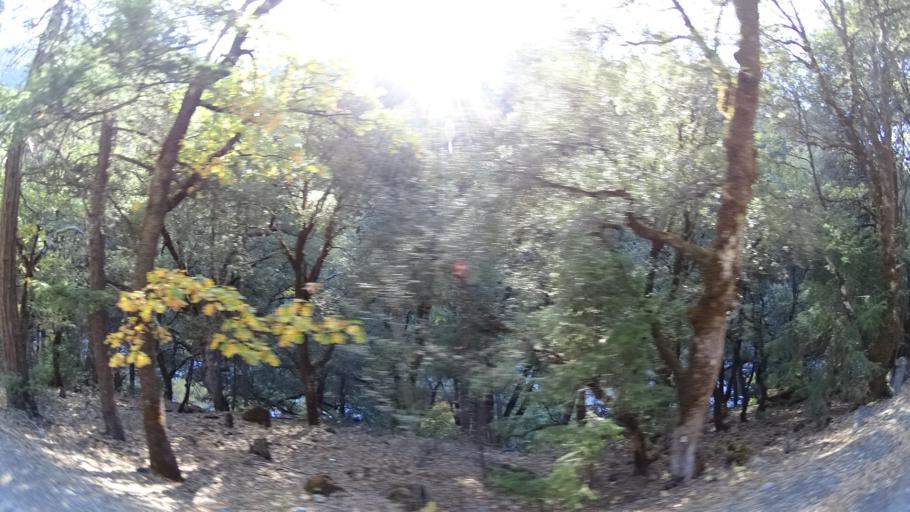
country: US
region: California
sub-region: Siskiyou County
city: Happy Camp
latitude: 41.6717
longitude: -123.1049
